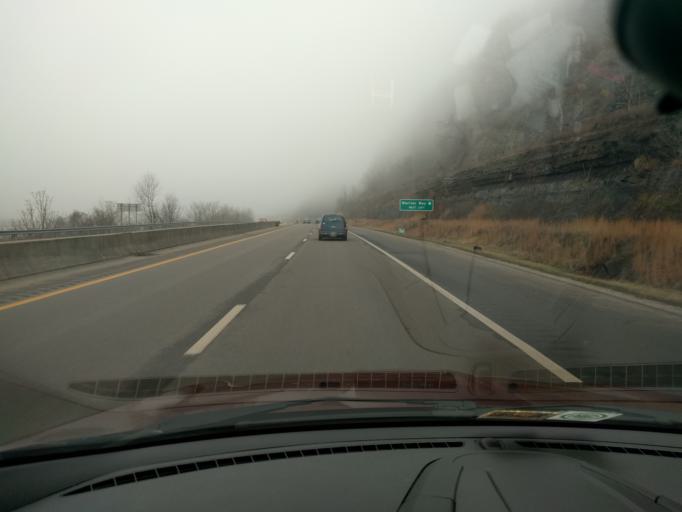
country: US
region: West Virginia
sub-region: Kanawha County
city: Chesapeake
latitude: 38.2085
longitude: -81.5067
